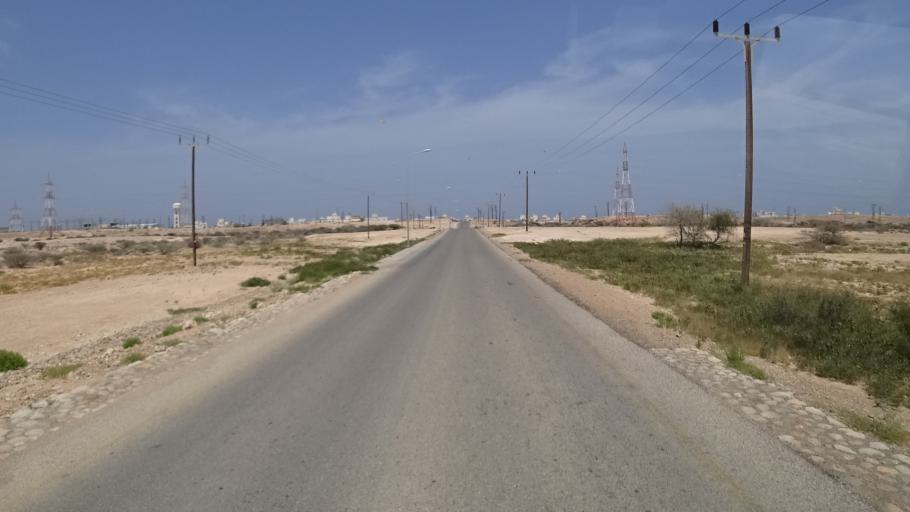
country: OM
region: Ash Sharqiyah
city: Sur
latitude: 22.6126
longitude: 59.4528
